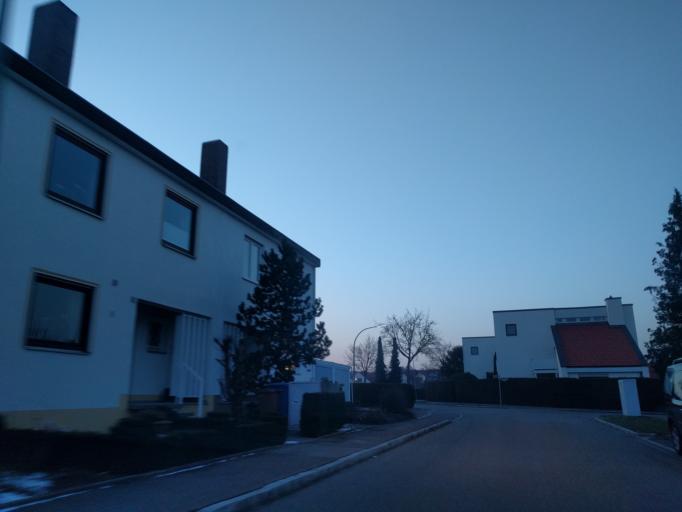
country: DE
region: Bavaria
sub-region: Swabia
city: Donauwoerth
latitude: 48.7167
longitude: 10.7500
